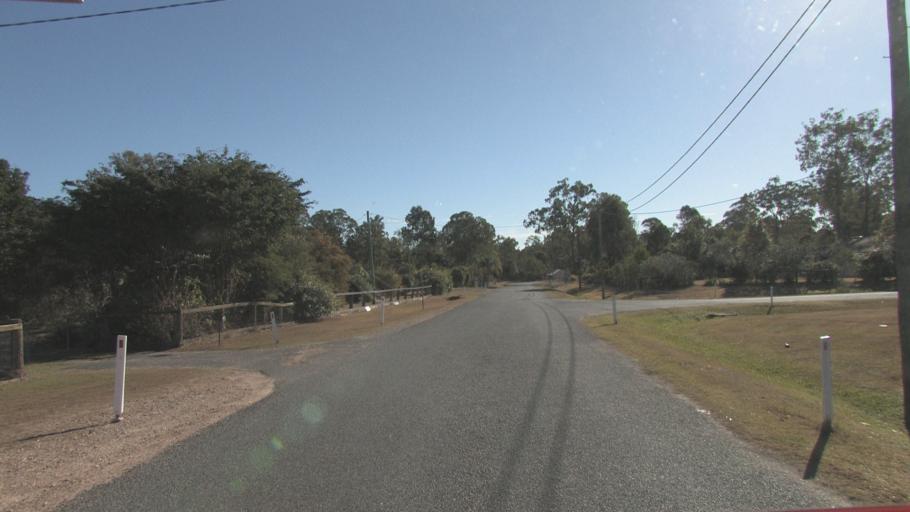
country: AU
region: Queensland
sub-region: Logan
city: North Maclean
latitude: -27.8042
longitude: 152.9784
